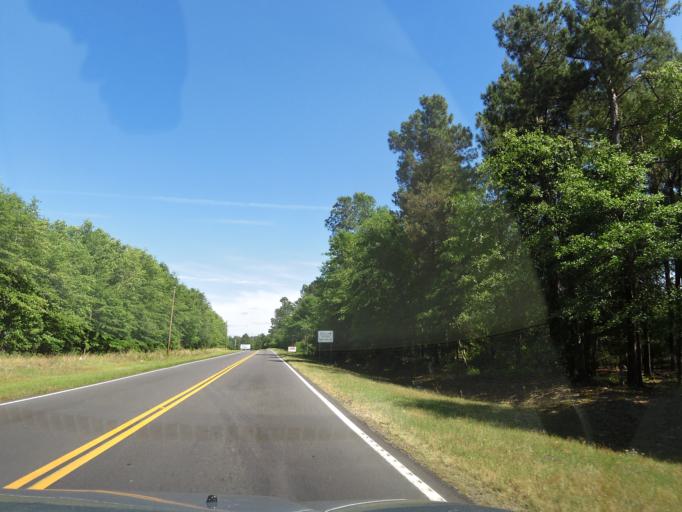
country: US
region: South Carolina
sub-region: Barnwell County
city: Williston
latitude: 33.4148
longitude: -81.4708
